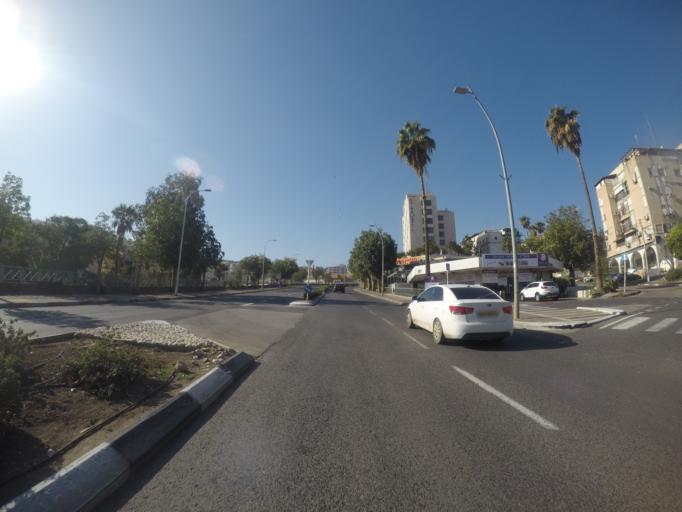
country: IL
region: Northern District
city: Tiberias
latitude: 32.7933
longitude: 35.5330
